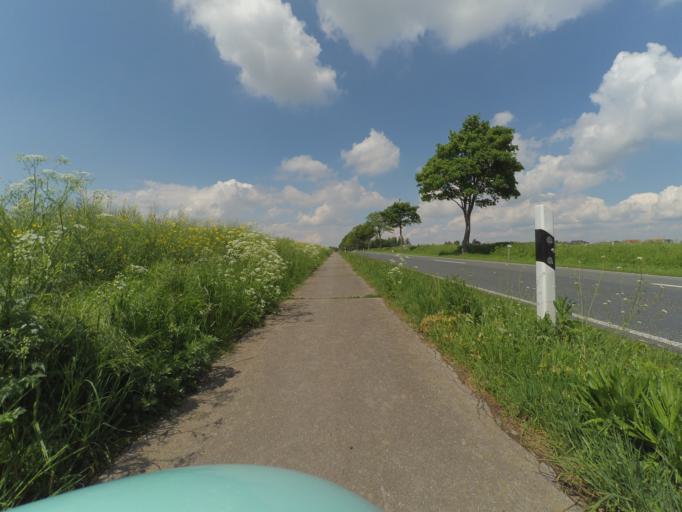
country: DE
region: Lower Saxony
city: Hohenhameln
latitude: 52.2547
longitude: 10.0806
